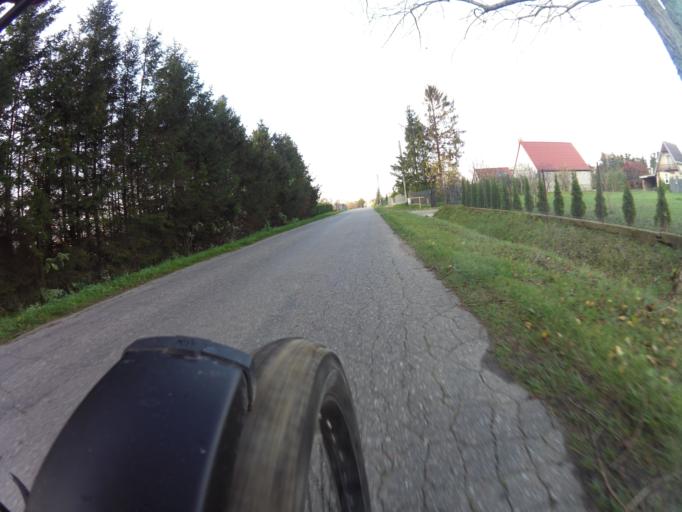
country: PL
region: Pomeranian Voivodeship
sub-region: Powiat pucki
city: Krokowa
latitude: 54.7574
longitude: 18.1839
